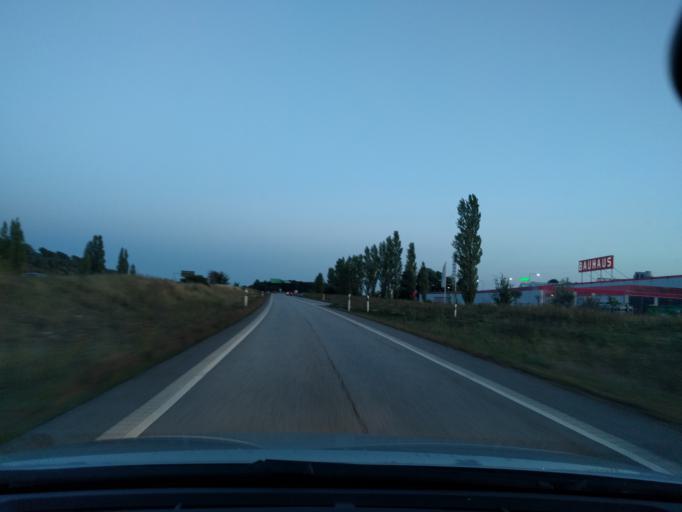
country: SE
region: Skane
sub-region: Malmo
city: Tygelsjo
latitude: 55.5533
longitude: 12.9992
